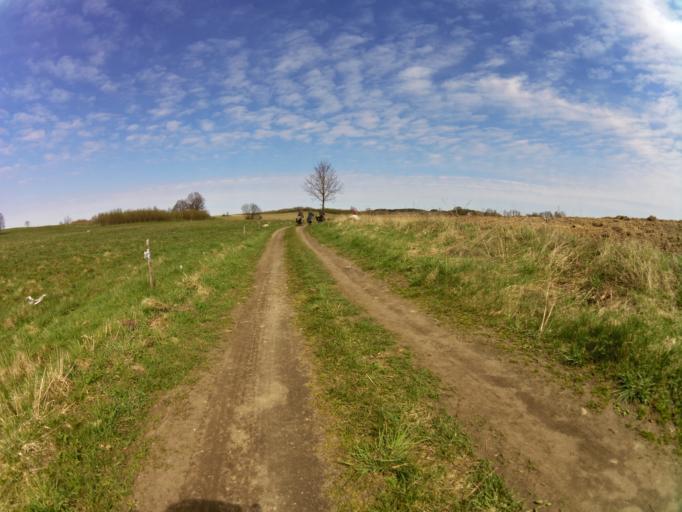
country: PL
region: West Pomeranian Voivodeship
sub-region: Powiat szczecinecki
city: Szczecinek
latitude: 53.7438
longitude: 16.5980
